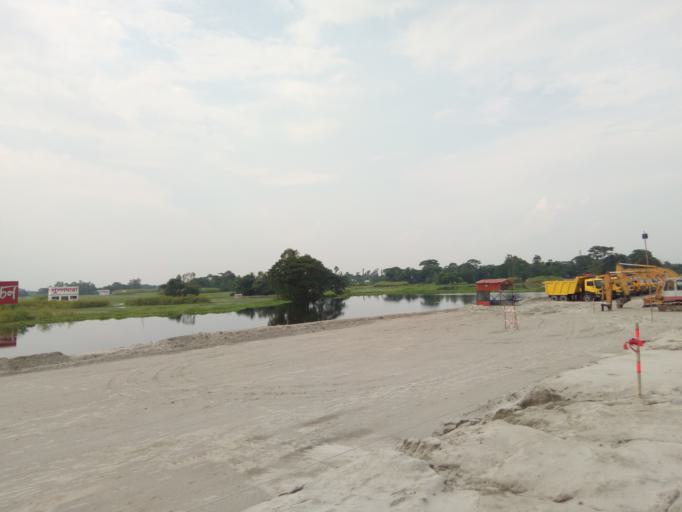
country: BD
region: Dhaka
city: Dohar
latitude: 23.5713
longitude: 90.3024
